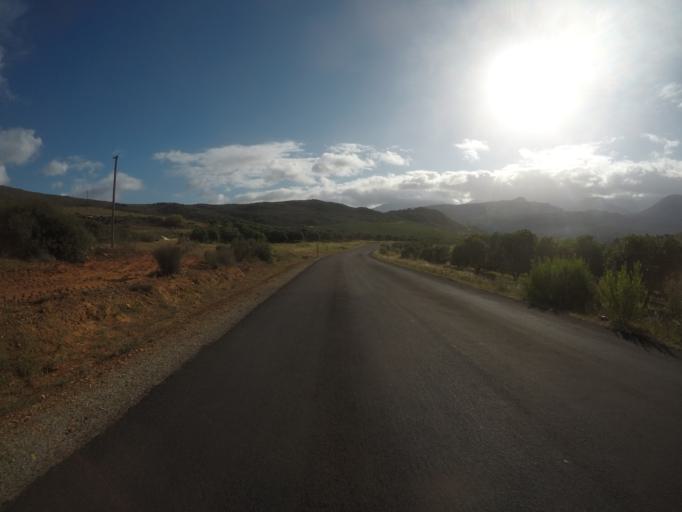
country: ZA
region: Western Cape
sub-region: West Coast District Municipality
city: Clanwilliam
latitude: -32.4325
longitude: 18.9484
